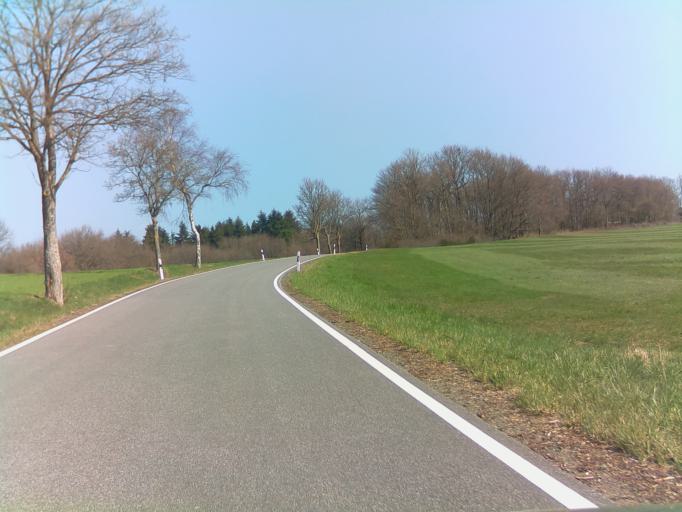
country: DE
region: Rheinland-Pfalz
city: Niederbrombach
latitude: 49.6913
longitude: 7.2564
